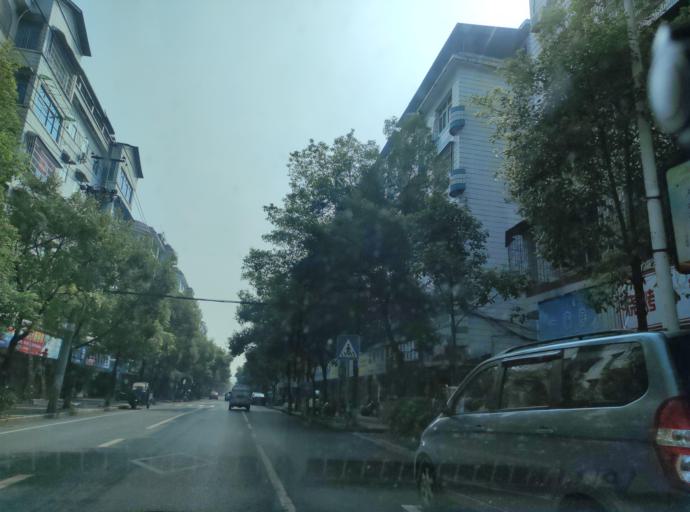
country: CN
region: Jiangxi Sheng
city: Pingxiang
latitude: 27.6441
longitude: 113.8554
